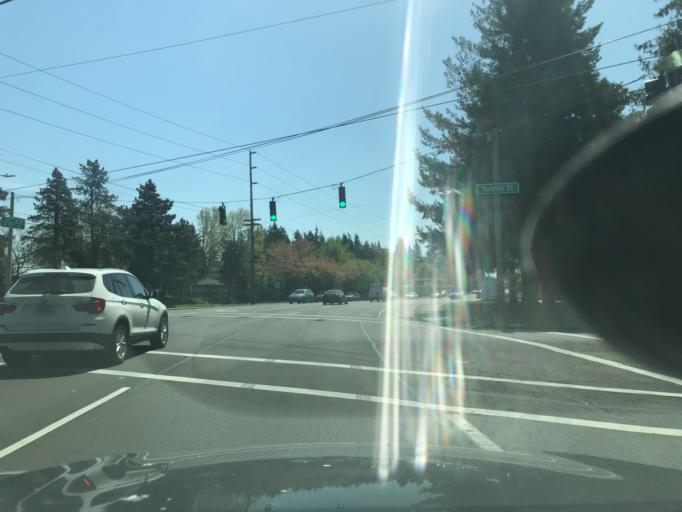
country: US
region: Oregon
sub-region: Multnomah County
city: Fairview
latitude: 45.5158
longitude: -122.4763
